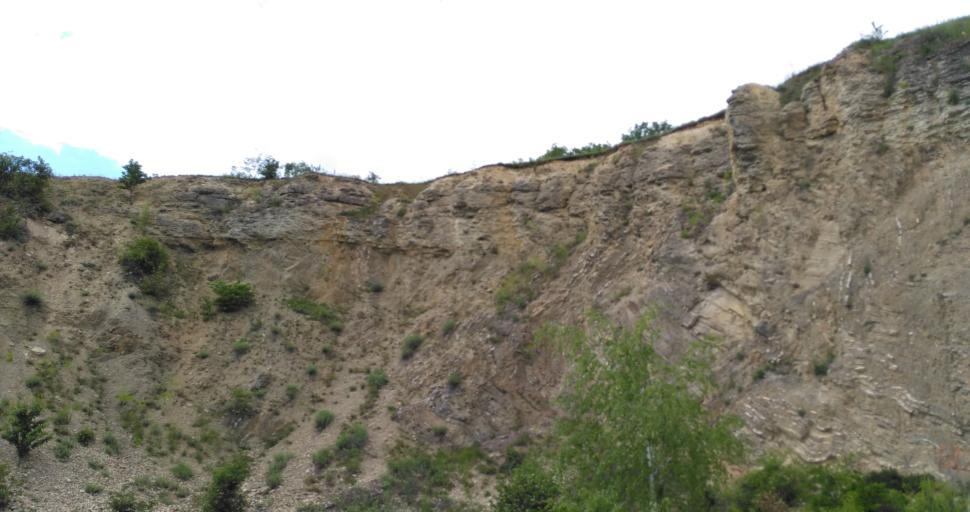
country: CZ
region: South Moravian
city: Bilovice nad Svitavou
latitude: 49.2203
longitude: 16.6717
